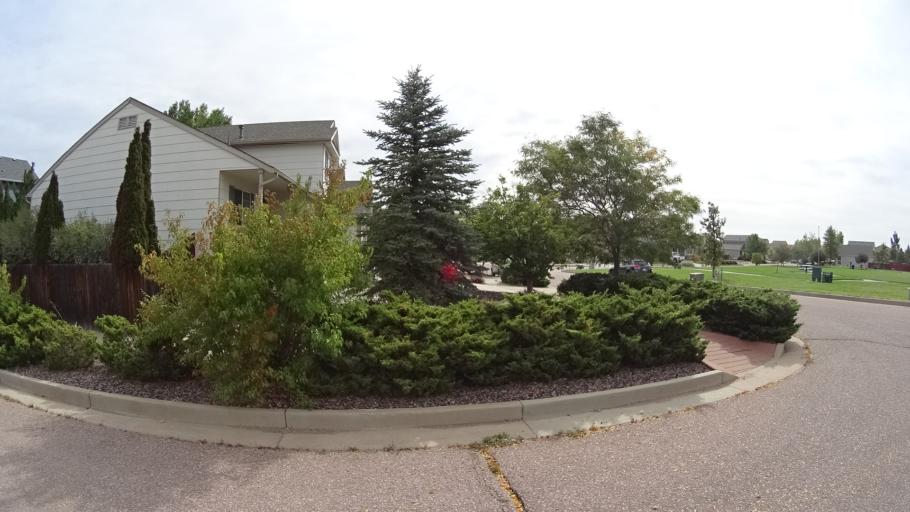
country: US
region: Colorado
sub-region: El Paso County
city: Cimarron Hills
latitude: 38.9211
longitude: -104.7139
